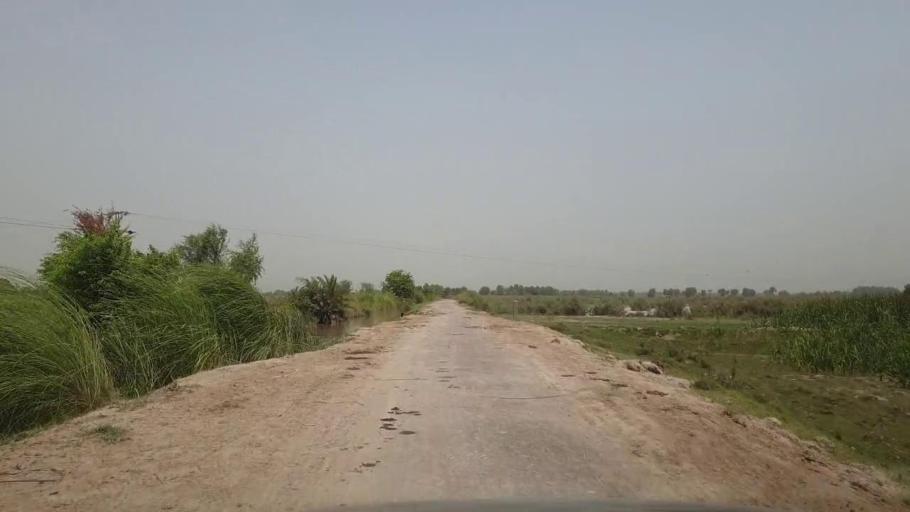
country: PK
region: Sindh
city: Gambat
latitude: 27.4484
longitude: 68.4437
